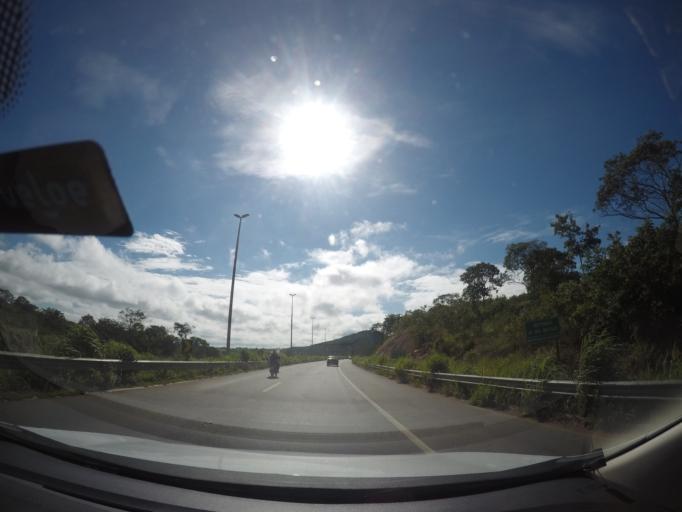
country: BR
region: Goias
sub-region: Senador Canedo
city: Senador Canedo
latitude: -16.6833
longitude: -49.1353
